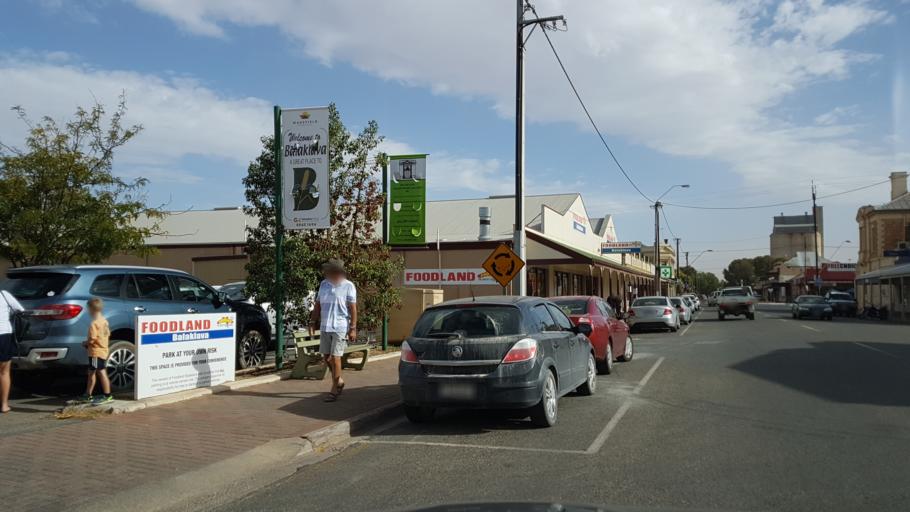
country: AU
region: South Australia
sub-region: Wakefield
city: Balaklava
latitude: -34.1468
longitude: 138.4154
